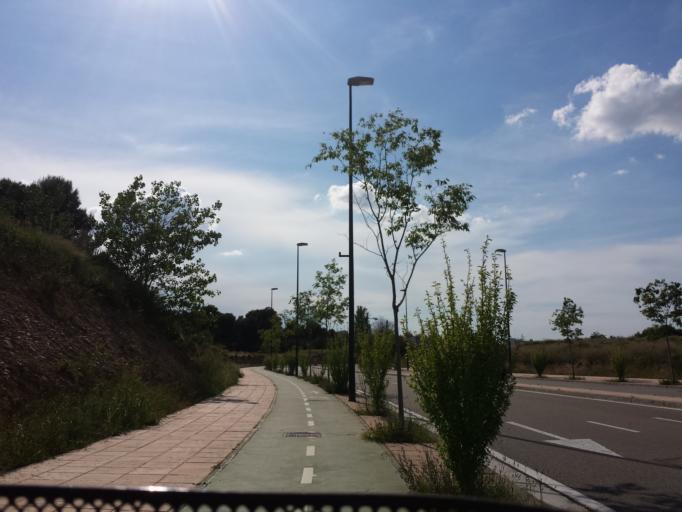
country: ES
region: Aragon
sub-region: Provincia de Zaragoza
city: Montecanal
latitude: 41.6340
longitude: -0.9354
